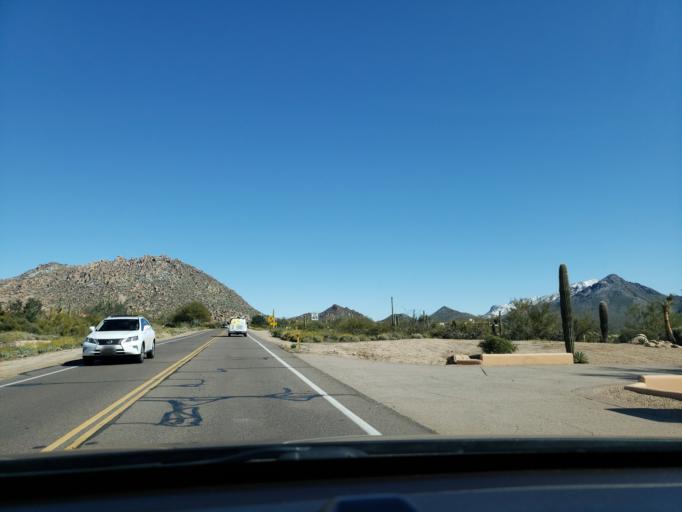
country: US
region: Arizona
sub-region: Maricopa County
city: Carefree
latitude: 33.7127
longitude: -111.8649
